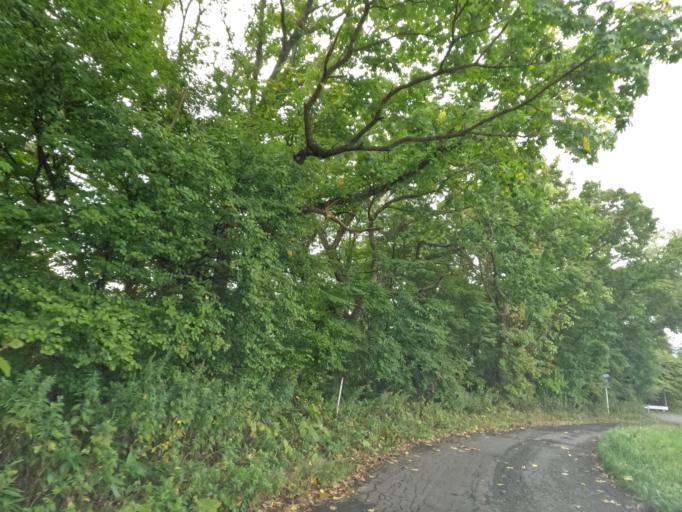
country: JP
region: Hokkaido
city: Date
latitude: 42.4928
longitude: 140.9026
